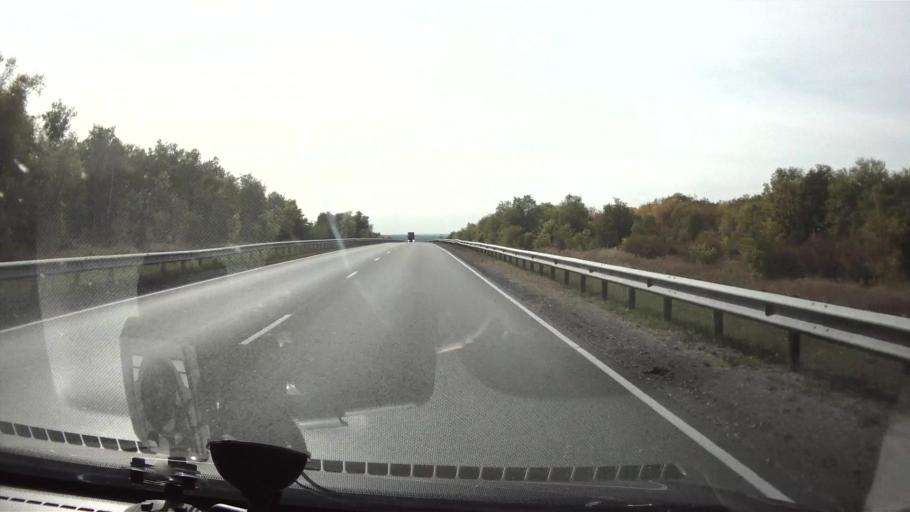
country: RU
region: Saratov
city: Balakovo
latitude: 52.0894
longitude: 47.6933
